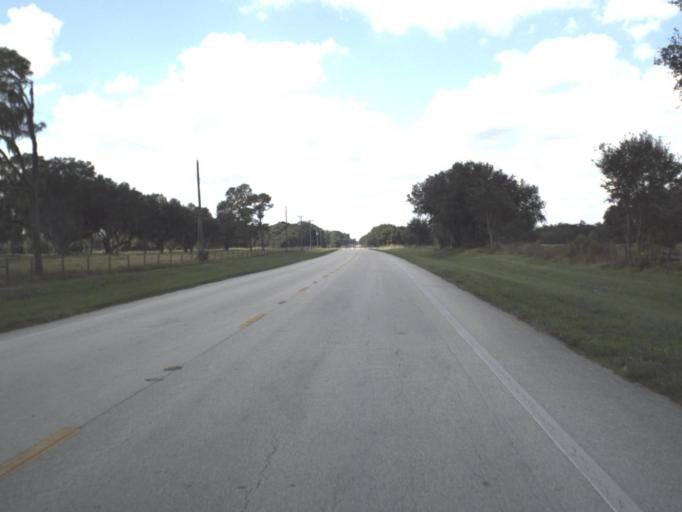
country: US
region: Florida
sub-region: Hardee County
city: Zolfo Springs
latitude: 27.4576
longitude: -81.6696
